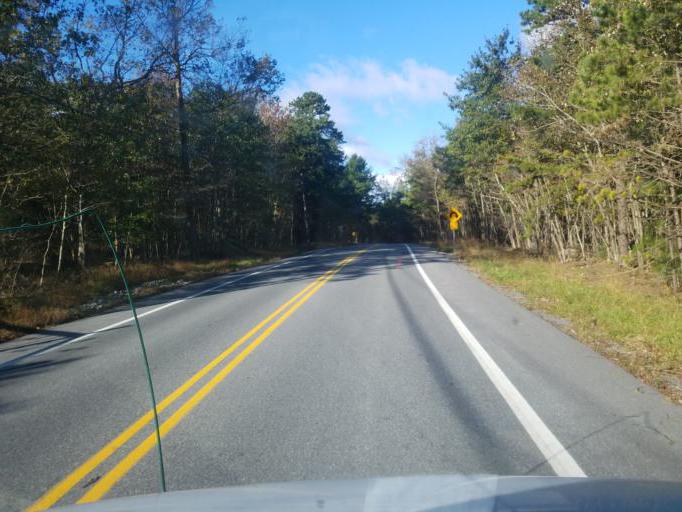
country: US
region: Pennsylvania
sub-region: Franklin County
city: Mont Alto
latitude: 39.8435
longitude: -77.5151
